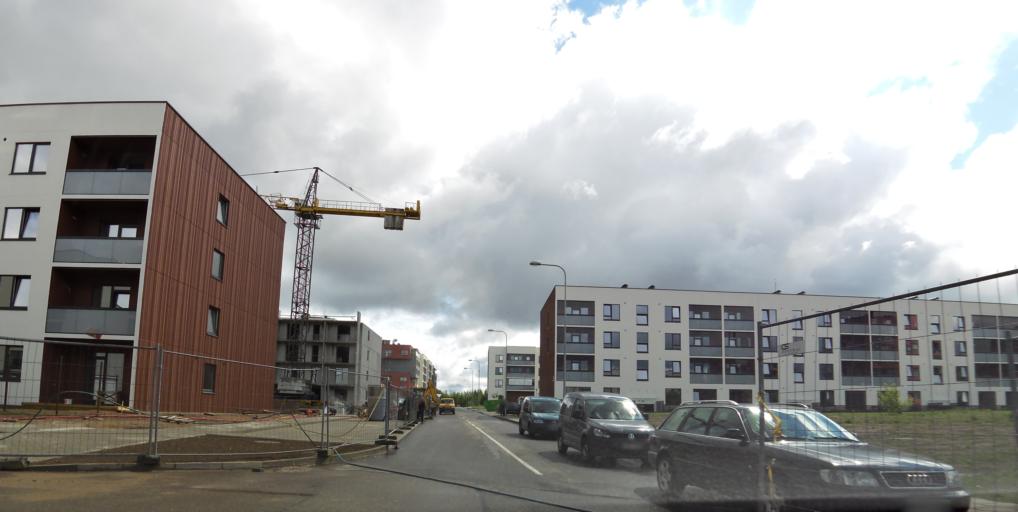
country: LT
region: Vilnius County
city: Pilaite
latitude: 54.7133
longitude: 25.1843
